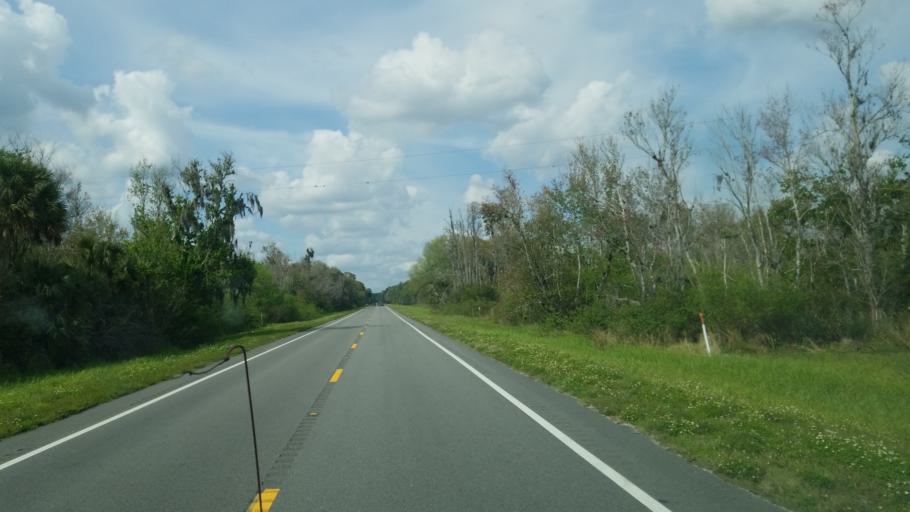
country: US
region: Florida
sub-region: Indian River County
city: Fellsmere
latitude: 27.7831
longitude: -80.9270
